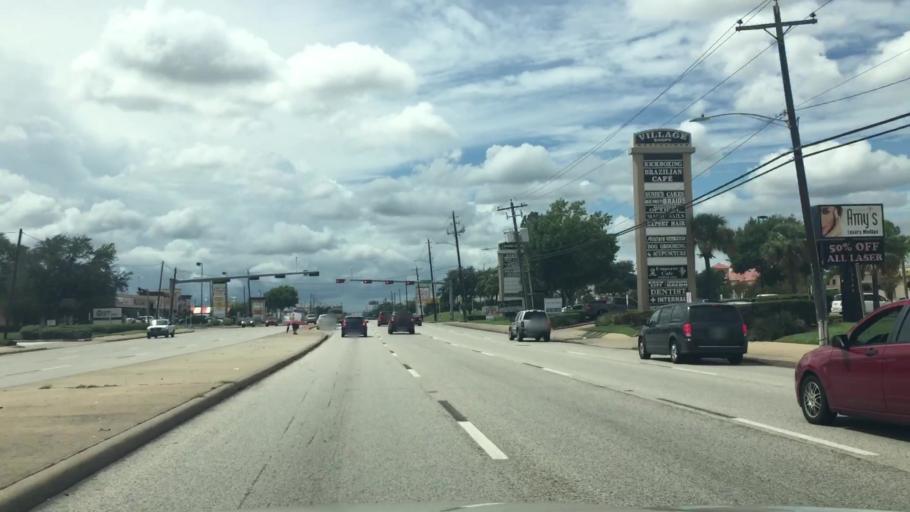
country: US
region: Texas
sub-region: Harris County
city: Bunker Hill Village
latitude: 29.7356
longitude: -95.5963
